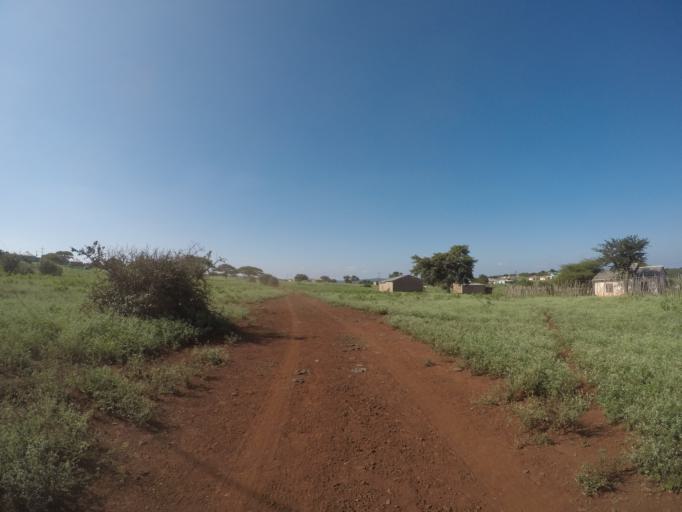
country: ZA
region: KwaZulu-Natal
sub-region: uThungulu District Municipality
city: Empangeni
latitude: -28.5739
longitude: 31.7282
